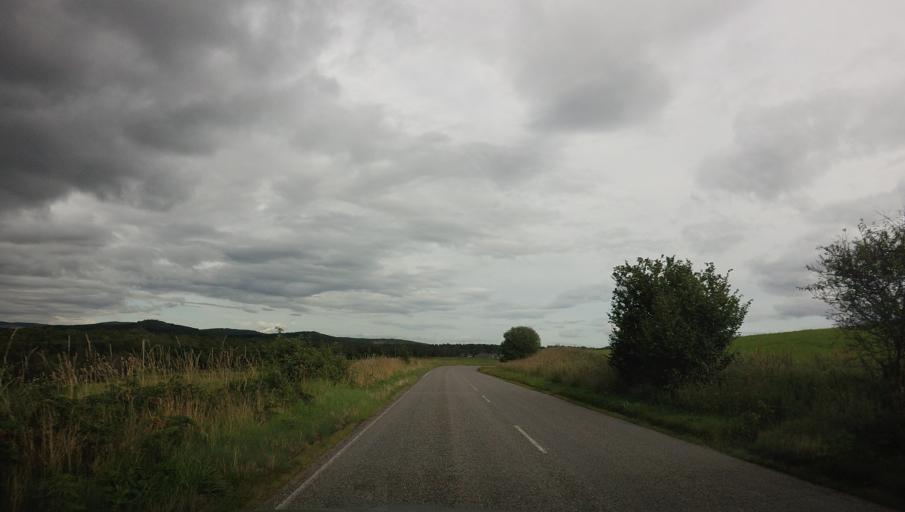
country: GB
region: Scotland
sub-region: Aberdeenshire
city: Ballater
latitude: 57.0762
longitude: -2.9184
